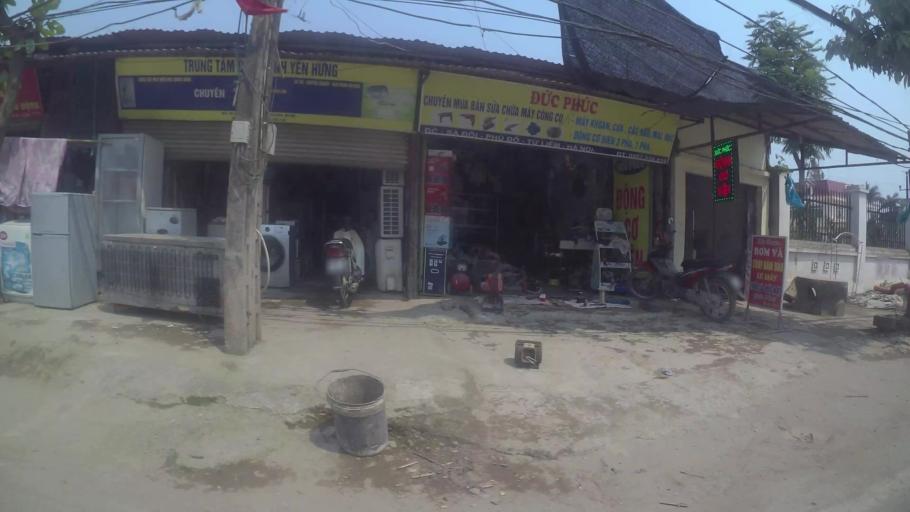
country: VN
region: Ha Noi
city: Ha Dong
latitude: 20.9996
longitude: 105.7647
